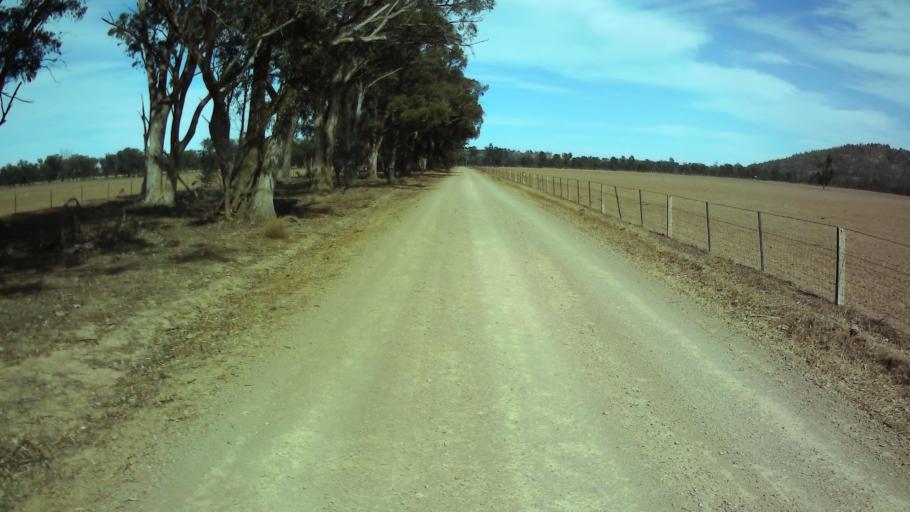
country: AU
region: New South Wales
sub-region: Weddin
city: Grenfell
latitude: -33.6861
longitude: 148.2992
